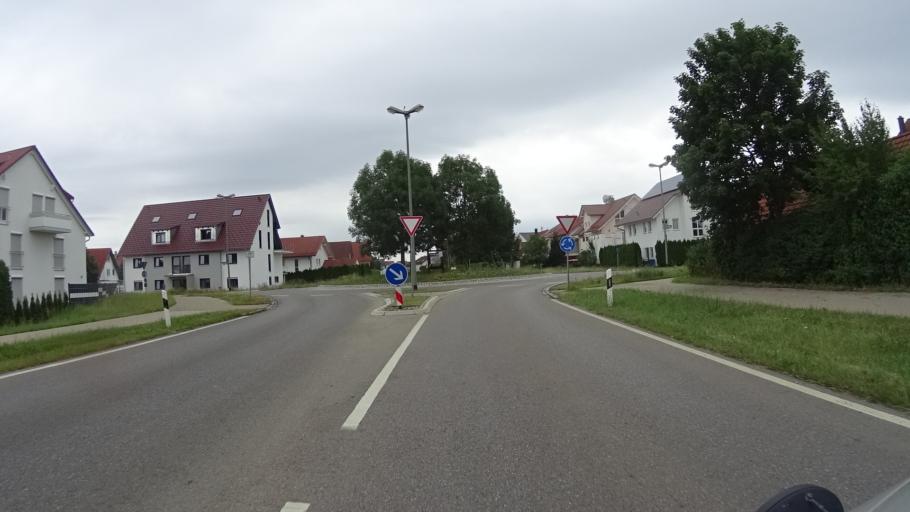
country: DE
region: Bavaria
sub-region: Swabia
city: Heimertingen
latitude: 48.0207
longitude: 10.1568
